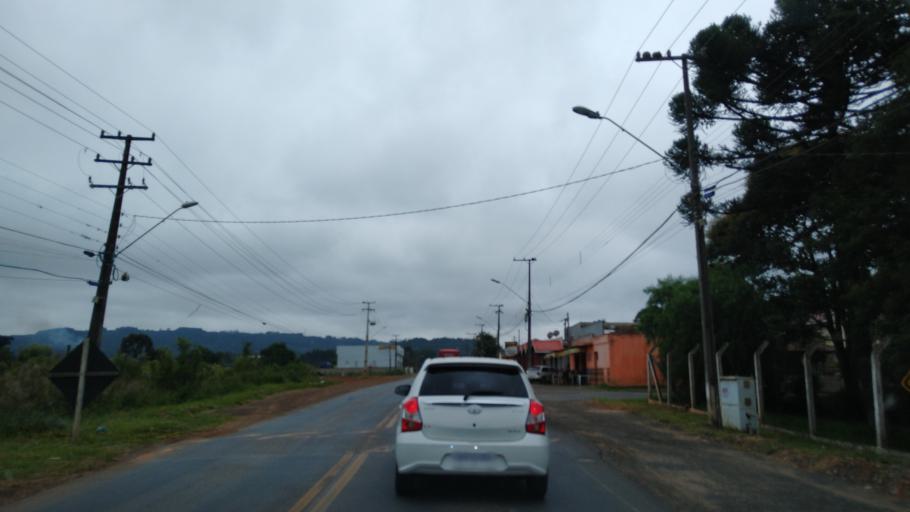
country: BR
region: Parana
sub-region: Uniao Da Vitoria
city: Uniao da Vitoria
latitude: -26.2457
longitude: -51.1218
